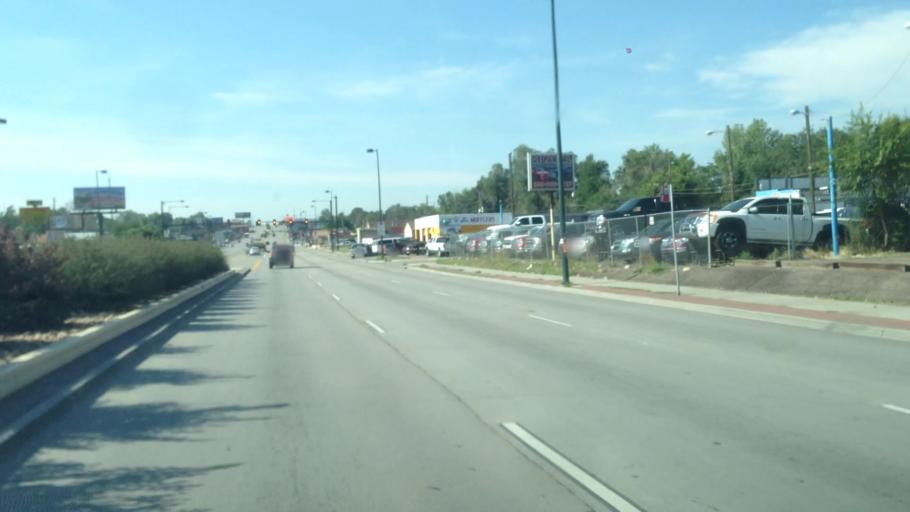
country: US
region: Colorado
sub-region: Denver County
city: Denver
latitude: 39.7221
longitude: -105.0252
